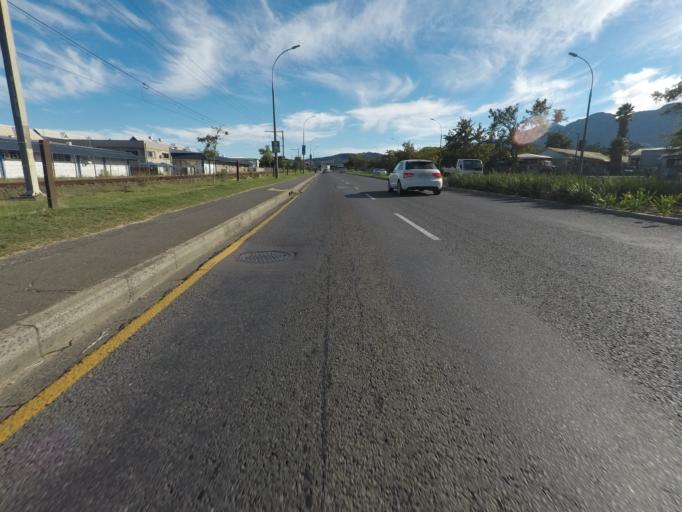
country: ZA
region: Western Cape
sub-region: Cape Winelands District Municipality
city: Stellenbosch
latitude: -33.9288
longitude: 18.8539
